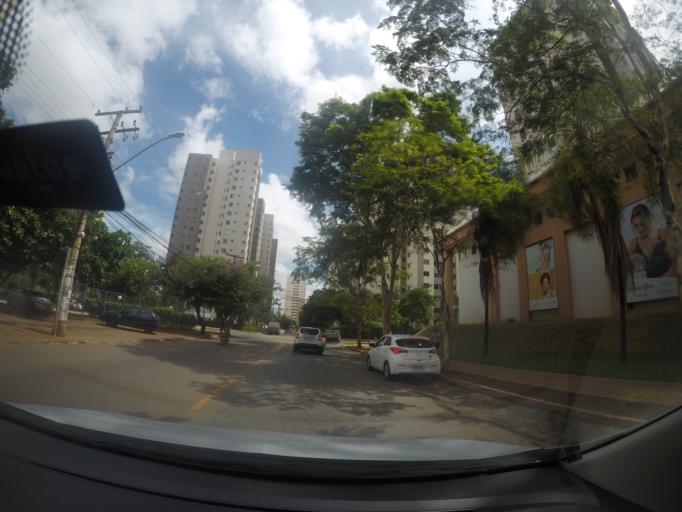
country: BR
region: Goias
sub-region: Goiania
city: Goiania
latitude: -16.7076
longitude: -49.3287
